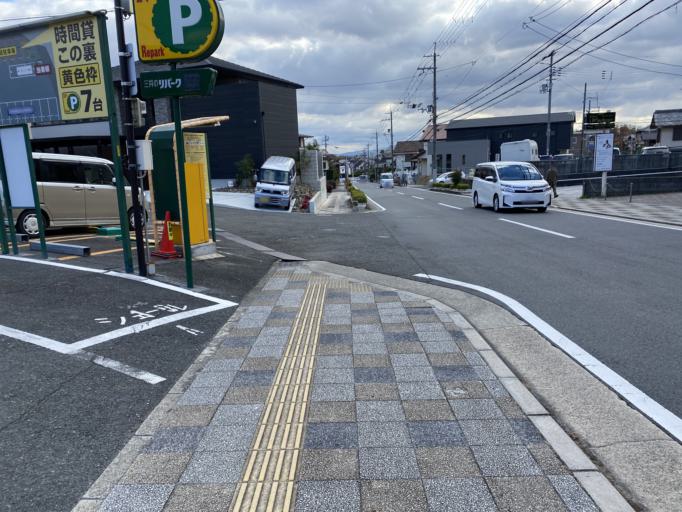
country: JP
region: Nara
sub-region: Ikoma-shi
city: Ikoma
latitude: 34.7139
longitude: 135.7452
